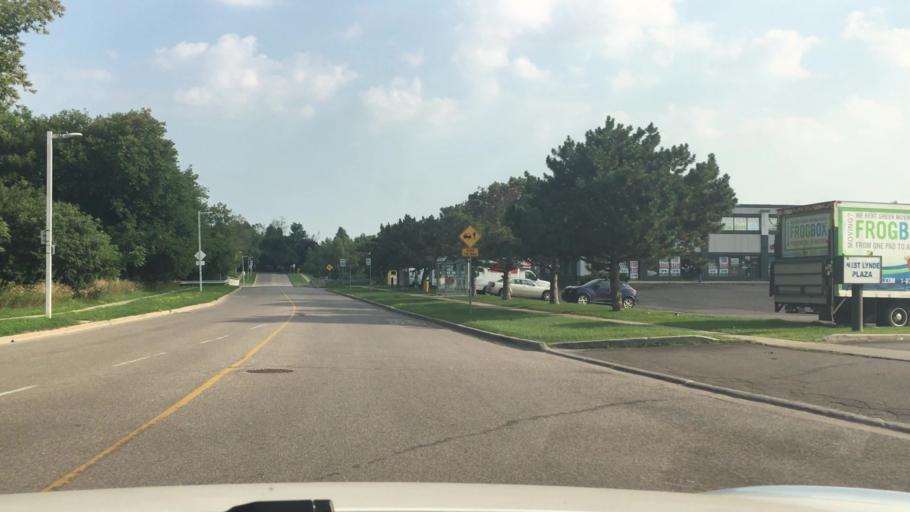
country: CA
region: Ontario
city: Ajax
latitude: 43.8750
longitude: -78.9616
